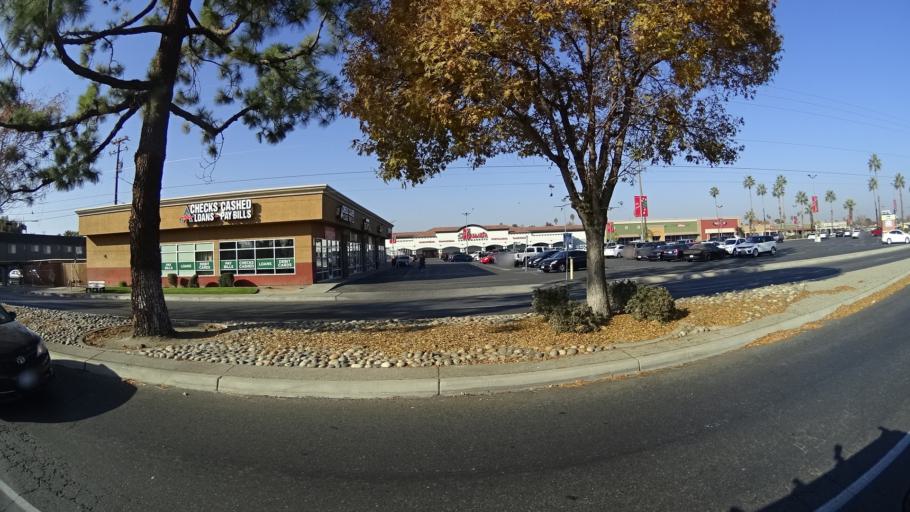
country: US
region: California
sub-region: Kern County
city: Bakersfield
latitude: 35.3301
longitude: -119.0211
